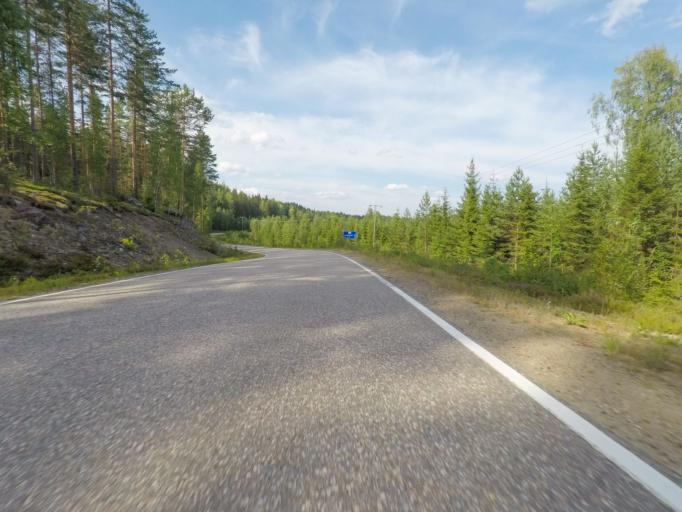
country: FI
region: Southern Savonia
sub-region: Savonlinna
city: Sulkava
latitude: 61.7246
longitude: 28.2056
